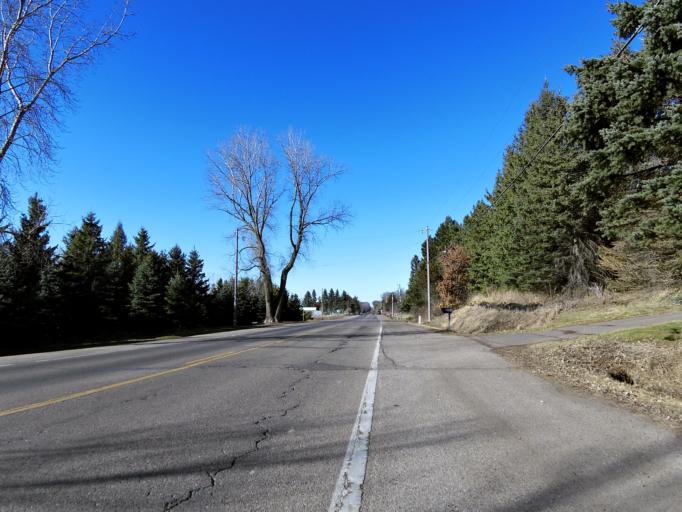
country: US
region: Minnesota
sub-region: Washington County
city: Oak Park Heights
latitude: 44.9893
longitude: -92.8223
